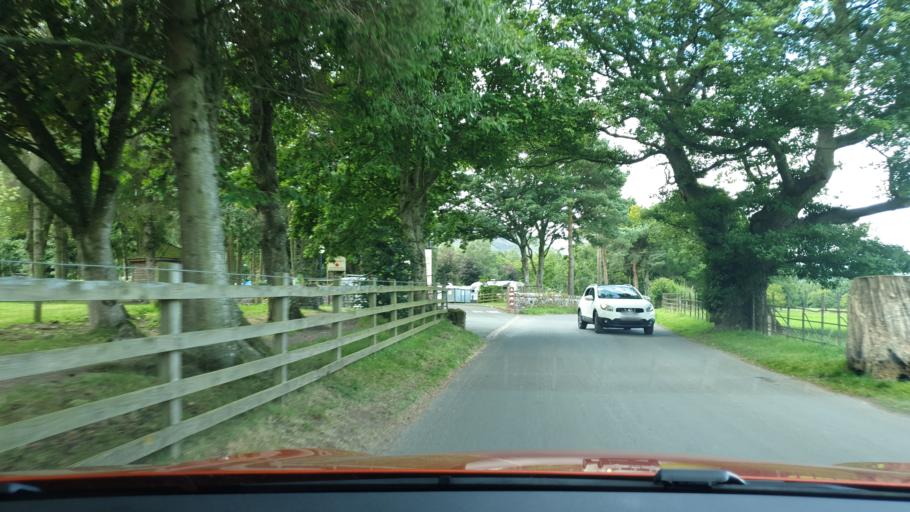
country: GB
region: England
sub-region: Cumbria
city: Penrith
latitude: 54.6037
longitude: -2.8239
